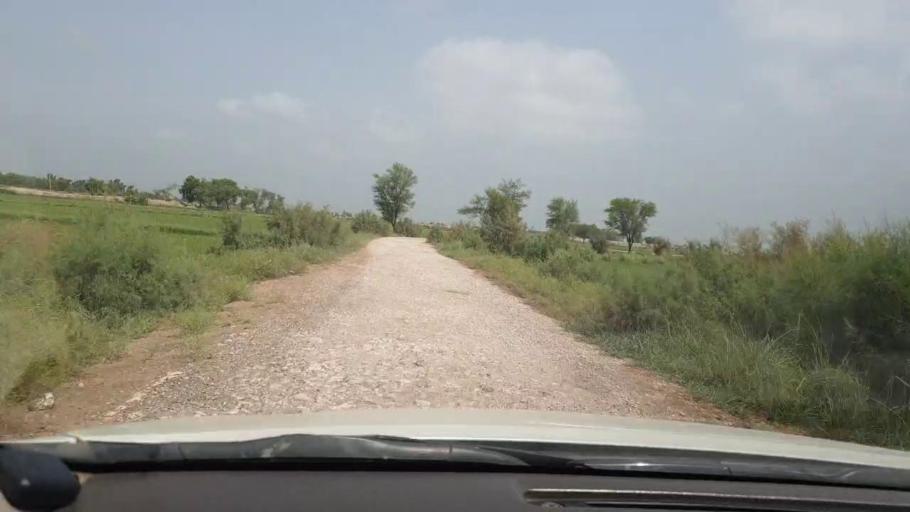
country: PK
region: Sindh
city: Garhi Yasin
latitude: 28.0099
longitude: 68.5397
